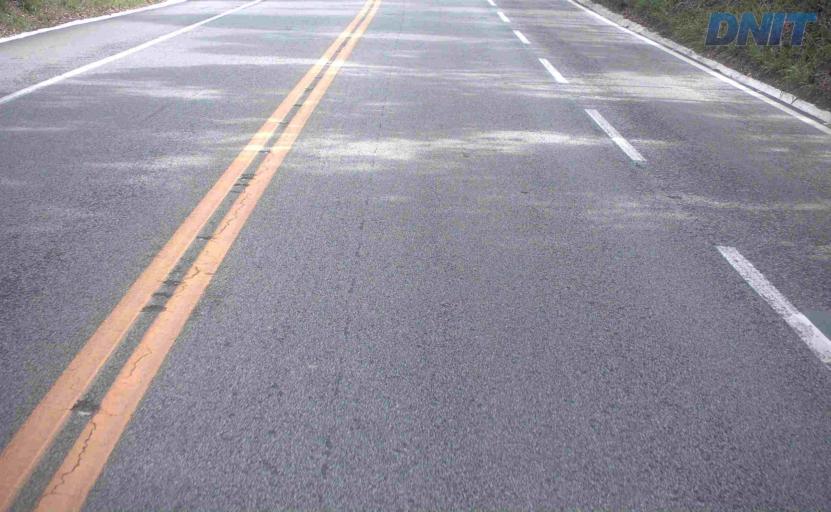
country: BR
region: Minas Gerais
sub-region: Caete
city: Caete
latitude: -19.7370
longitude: -43.6019
